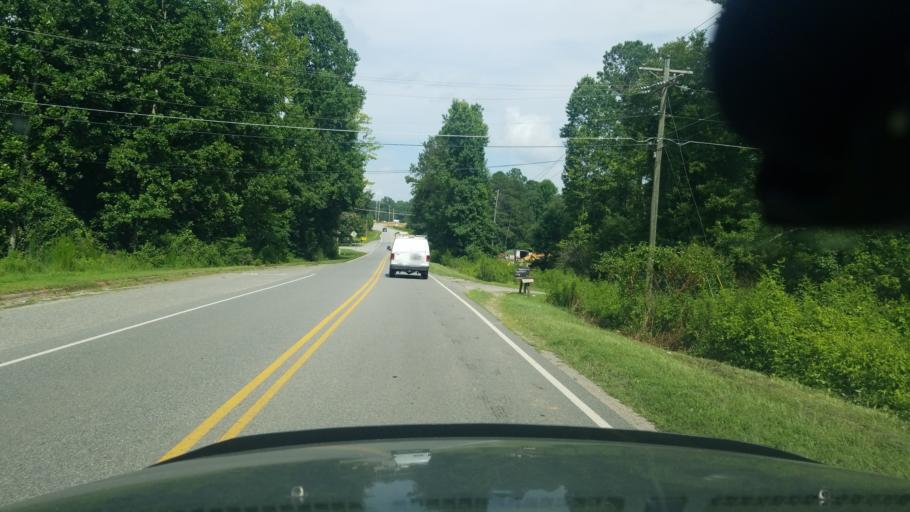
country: US
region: Georgia
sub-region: Dawson County
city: Dawsonville
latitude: 34.3121
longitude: -84.0718
